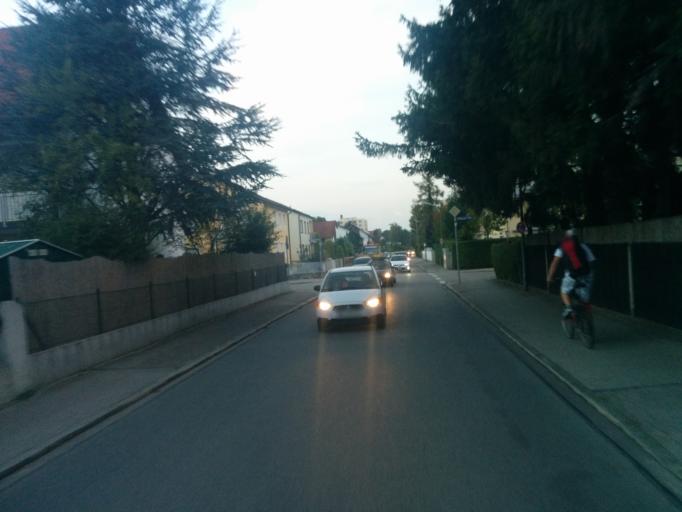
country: DE
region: Bavaria
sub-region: Upper Bavaria
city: Karlsfeld
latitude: 48.1804
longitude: 11.4898
